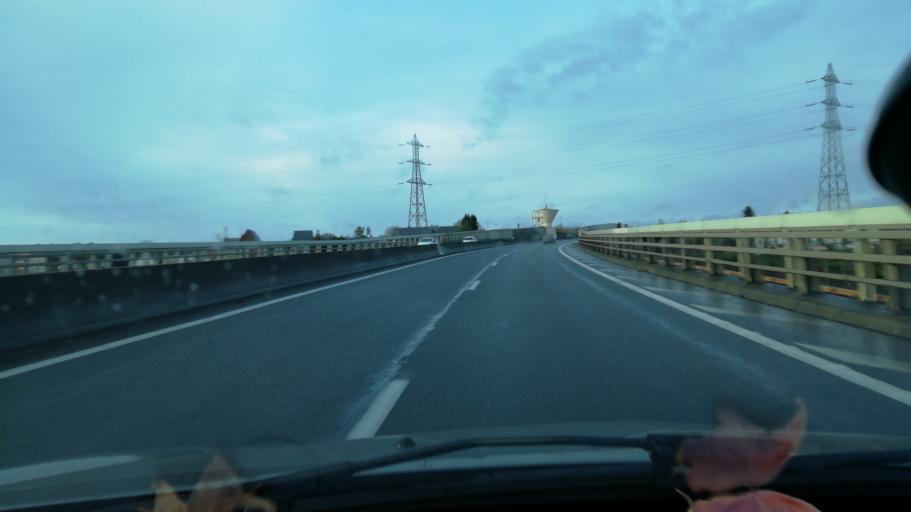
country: FR
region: Nord-Pas-de-Calais
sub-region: Departement du Nord
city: Hautmont
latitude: 50.2625
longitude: 3.9270
